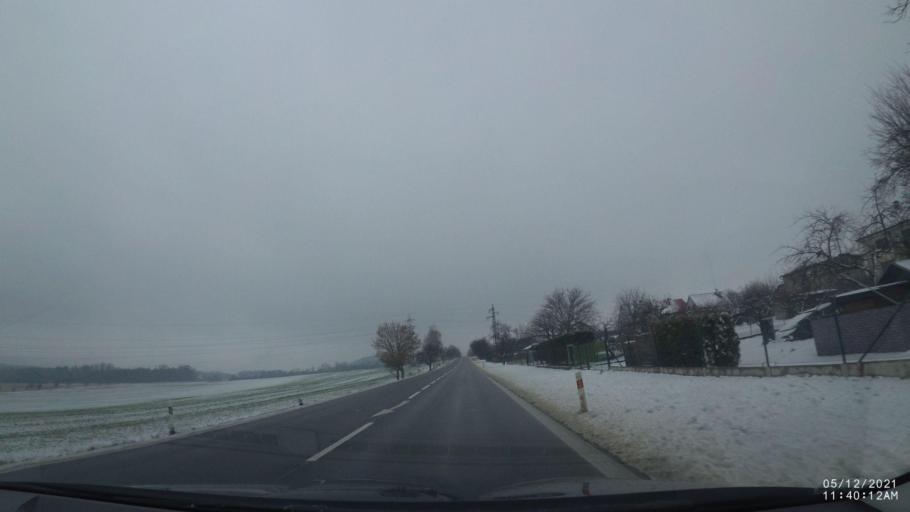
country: CZ
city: Dobruska
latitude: 50.2597
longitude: 16.2091
